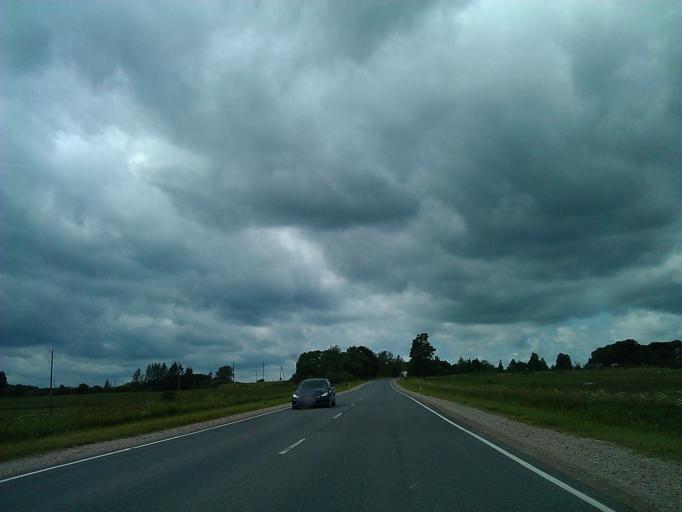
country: LV
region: Engure
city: Smarde
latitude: 56.9207
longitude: 23.2746
